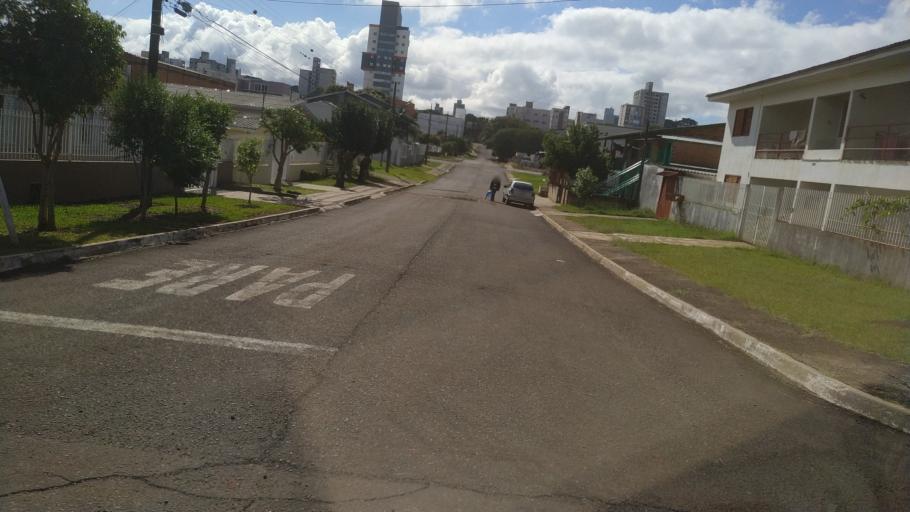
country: BR
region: Santa Catarina
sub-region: Chapeco
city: Chapeco
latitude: -27.0970
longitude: -52.6356
